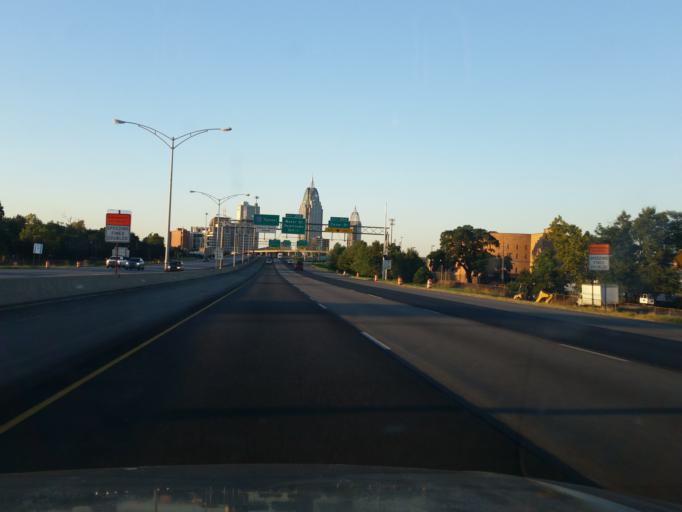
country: US
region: Alabama
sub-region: Mobile County
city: Mobile
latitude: 30.6780
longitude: -88.0434
